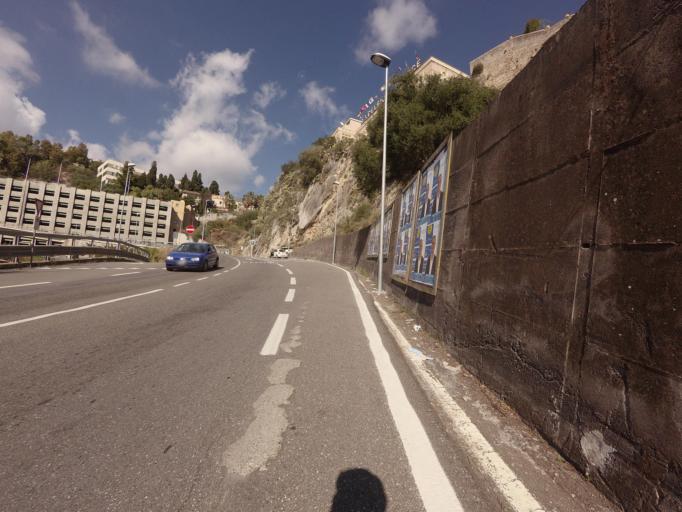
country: IT
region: Sicily
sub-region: Messina
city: Taormina
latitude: 37.8496
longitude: 15.2806
